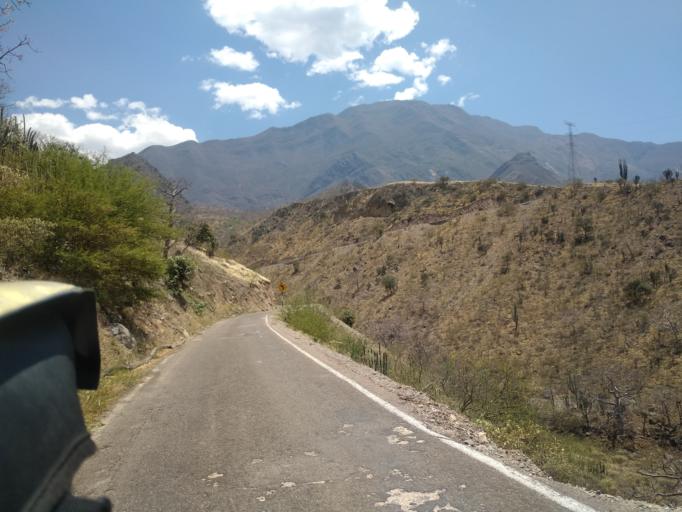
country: PE
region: Amazonas
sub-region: Provincia de Chachapoyas
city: Balsas
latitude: -6.8518
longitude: -78.0367
